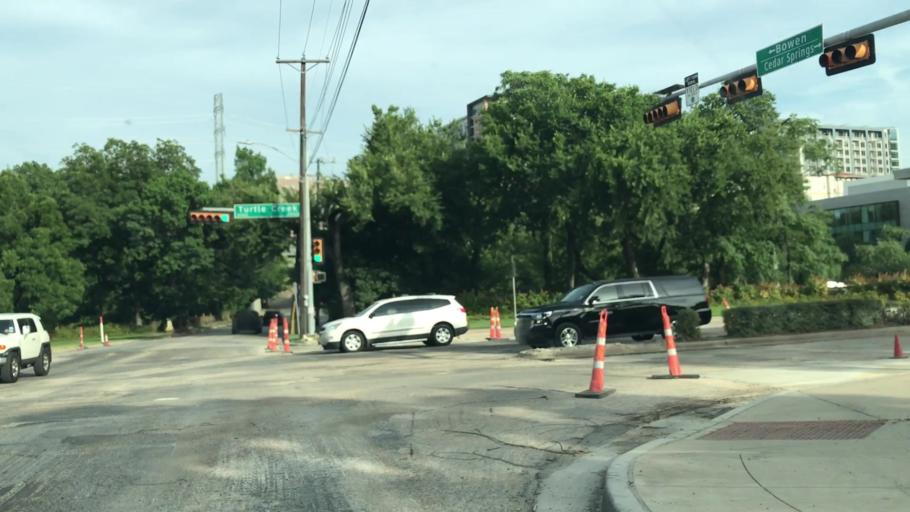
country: US
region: Texas
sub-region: Dallas County
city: Dallas
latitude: 32.8057
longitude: -96.8044
